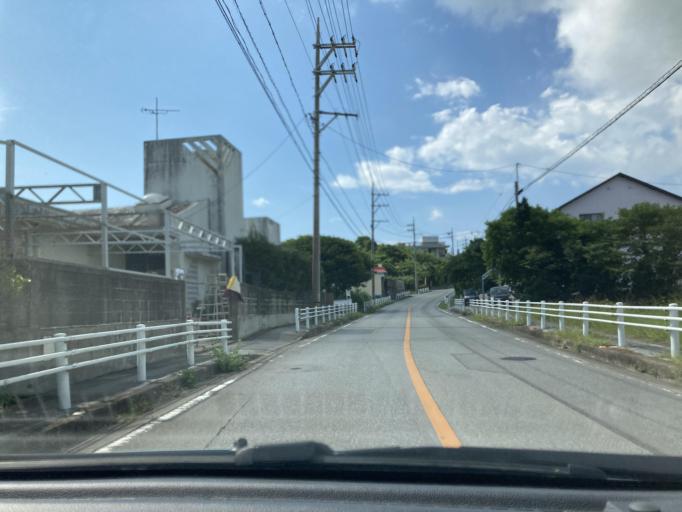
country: JP
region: Okinawa
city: Tomigusuku
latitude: 26.1506
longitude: 127.7917
